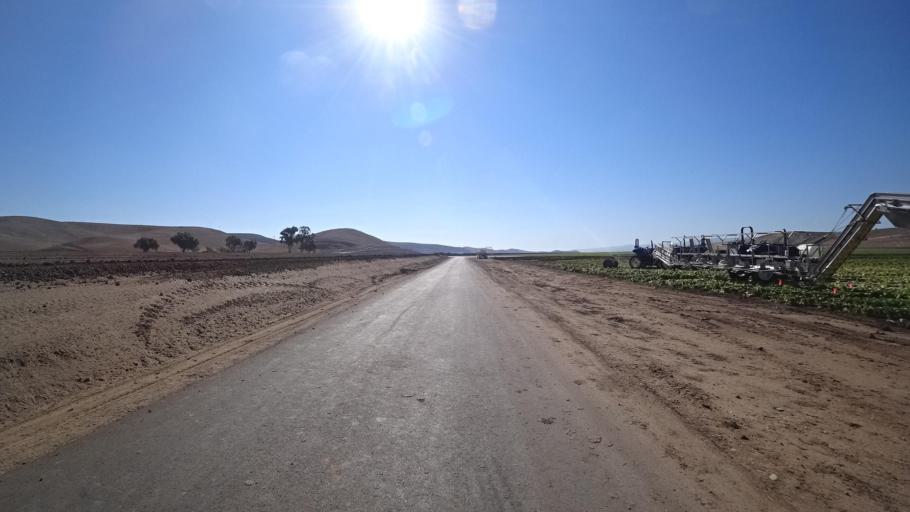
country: US
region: California
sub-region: Monterey County
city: King City
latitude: 36.1558
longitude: -121.0185
